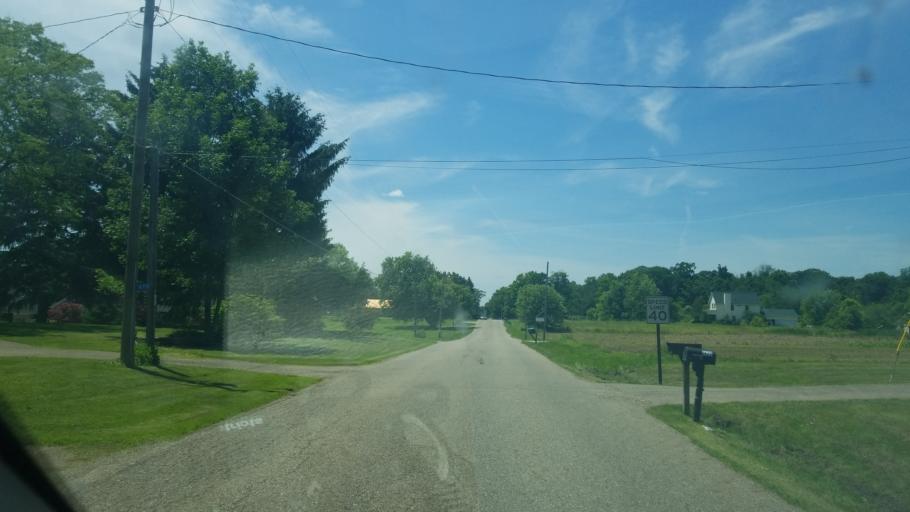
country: US
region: Ohio
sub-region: Stark County
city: Alliance
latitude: 40.8576
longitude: -81.1208
